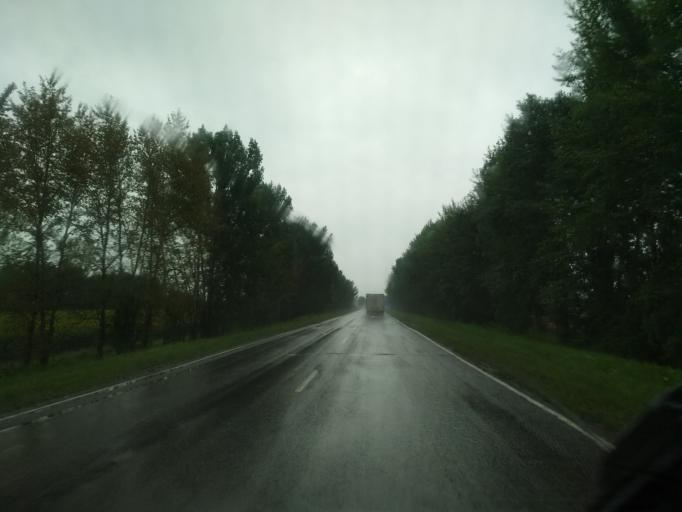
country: RU
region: Voronezj
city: Verkhnyaya Khava
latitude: 51.6859
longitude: 39.9178
